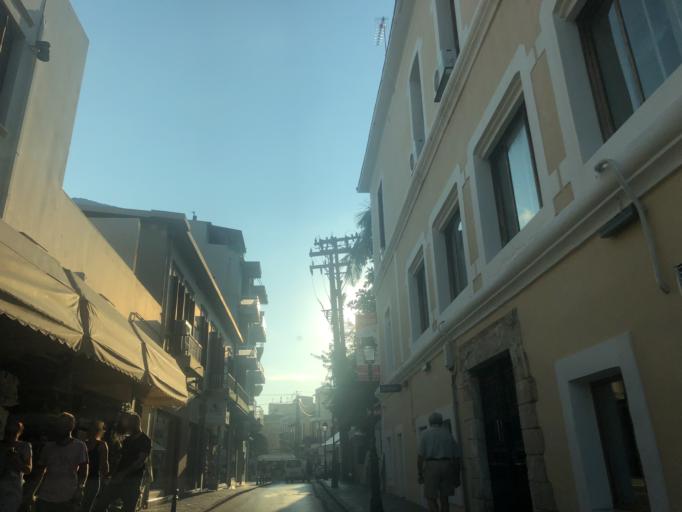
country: GR
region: Crete
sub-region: Nomos Rethymnis
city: Rethymno
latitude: 35.3699
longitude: 24.4766
